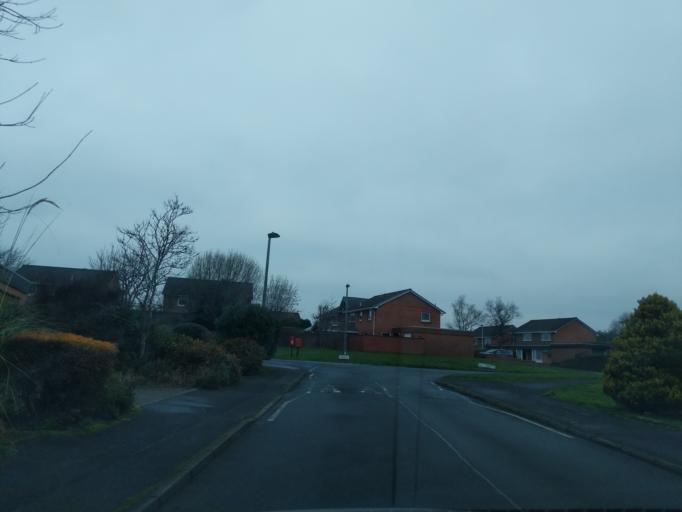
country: GB
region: Scotland
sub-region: Edinburgh
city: Balerno
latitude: 55.8926
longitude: -3.3340
